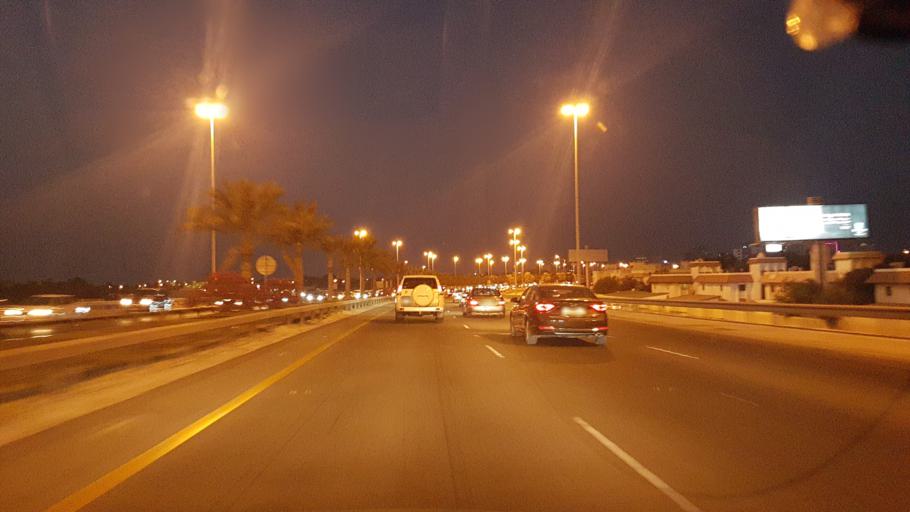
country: BH
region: Manama
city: Jidd Hafs
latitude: 26.2196
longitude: 50.5218
